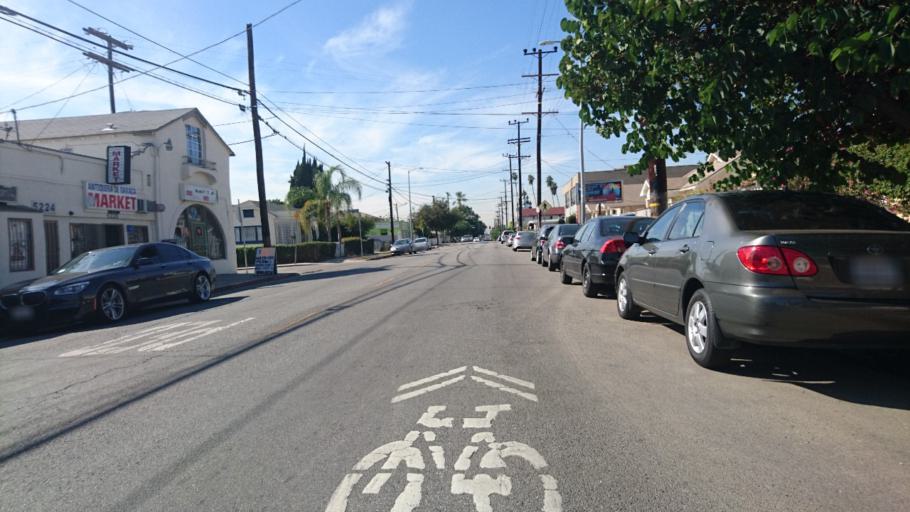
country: US
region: California
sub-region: Los Angeles County
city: Hollywood
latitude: 34.0952
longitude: -118.3033
